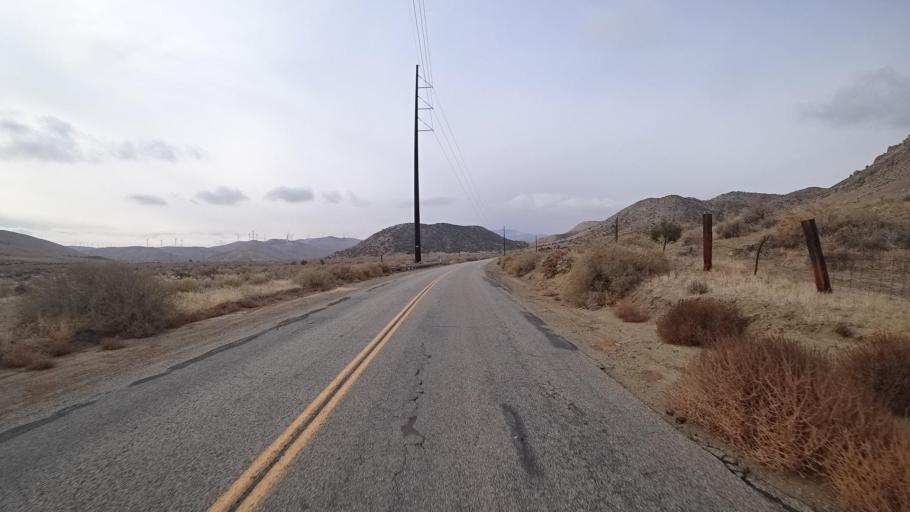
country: US
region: California
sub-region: Kern County
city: Tehachapi
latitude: 35.1391
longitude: -118.3177
